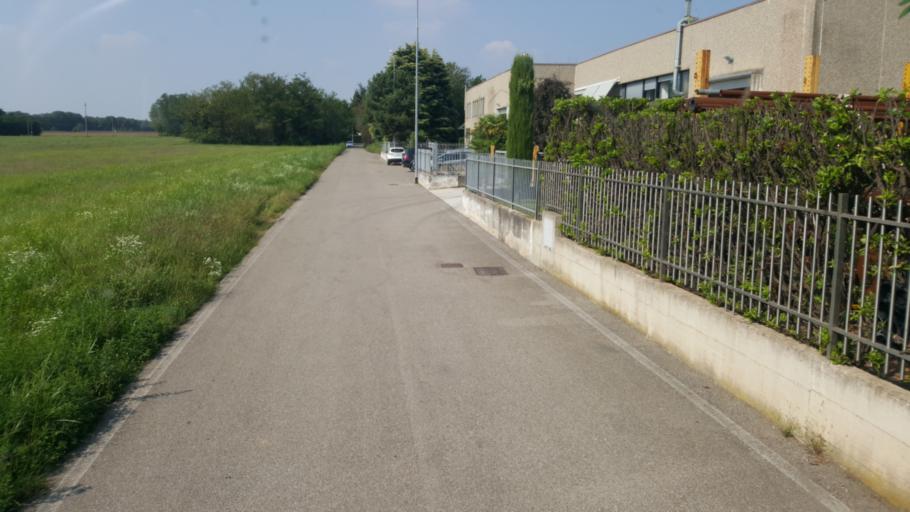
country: IT
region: Lombardy
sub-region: Provincia di Como
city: Locate Varesino
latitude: 45.6734
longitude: 8.9243
